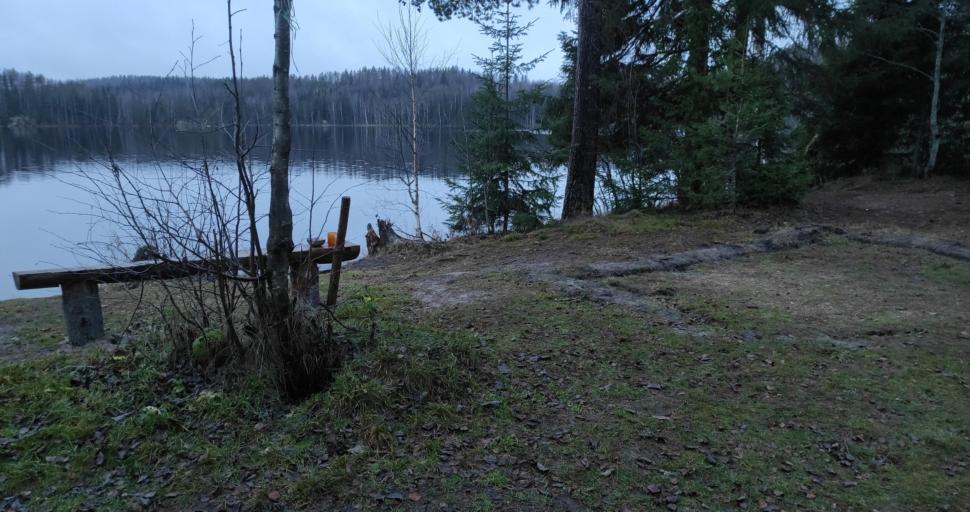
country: RU
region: Republic of Karelia
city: Pitkyaranta
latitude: 61.7552
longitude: 31.3341
